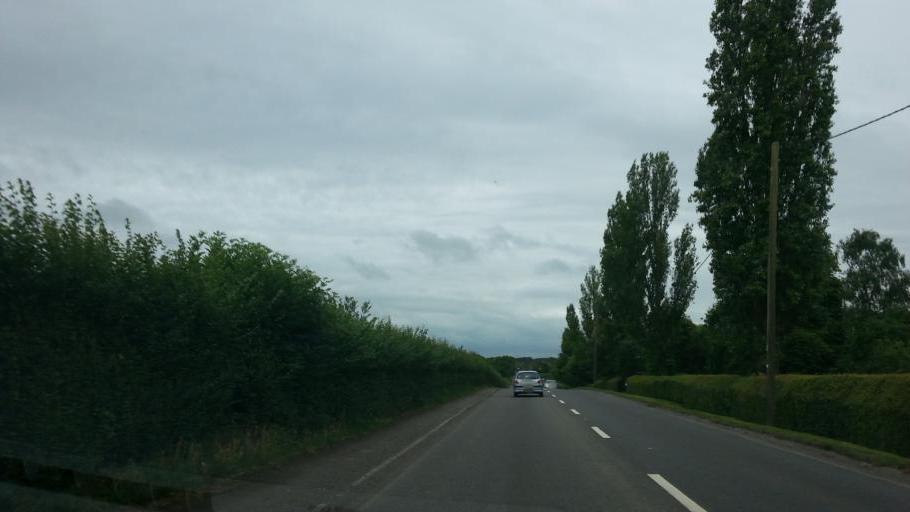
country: GB
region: England
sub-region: Wiltshire
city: North Bradley
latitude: 51.2973
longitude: -2.1838
